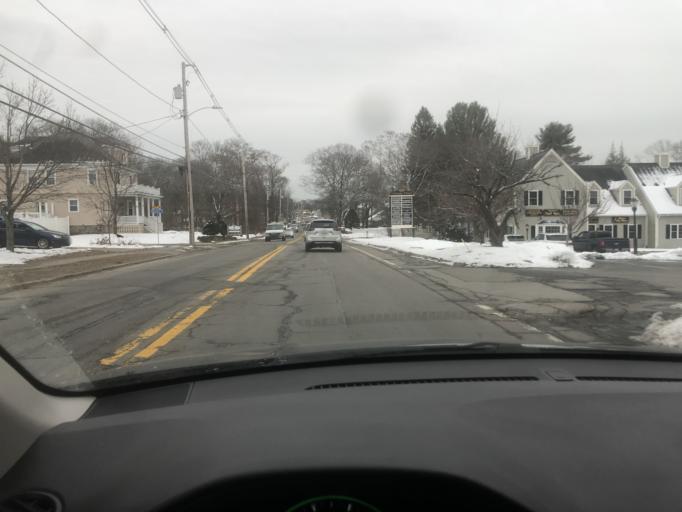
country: US
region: Massachusetts
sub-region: Middlesex County
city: Tewksbury
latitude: 42.6091
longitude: -71.2295
